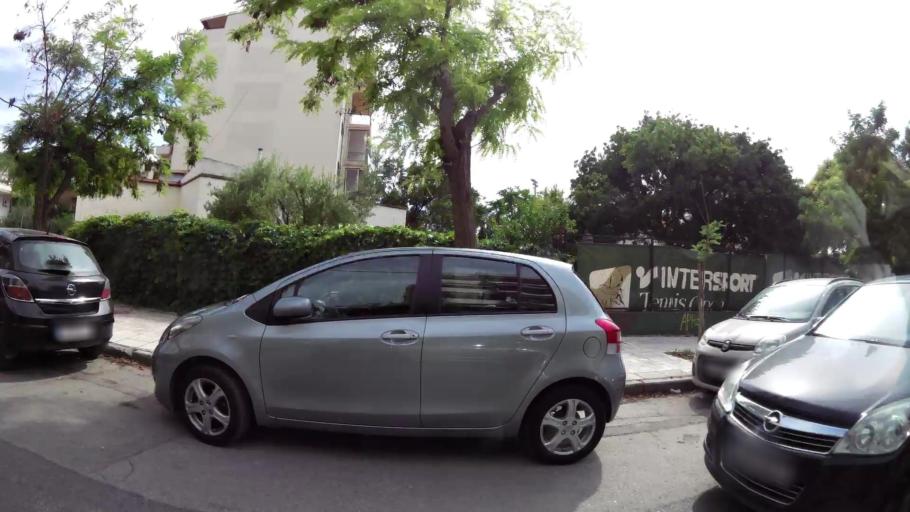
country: GR
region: Central Macedonia
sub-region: Nomos Thessalonikis
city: Kalamaria
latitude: 40.5908
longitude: 22.9571
